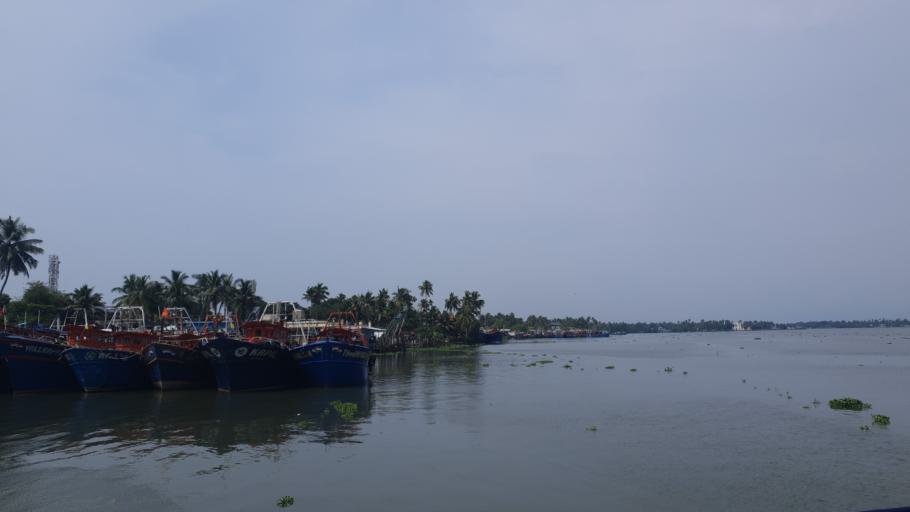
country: IN
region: Kerala
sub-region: Ernakulam
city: Cochin
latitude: 9.9877
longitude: 76.2408
